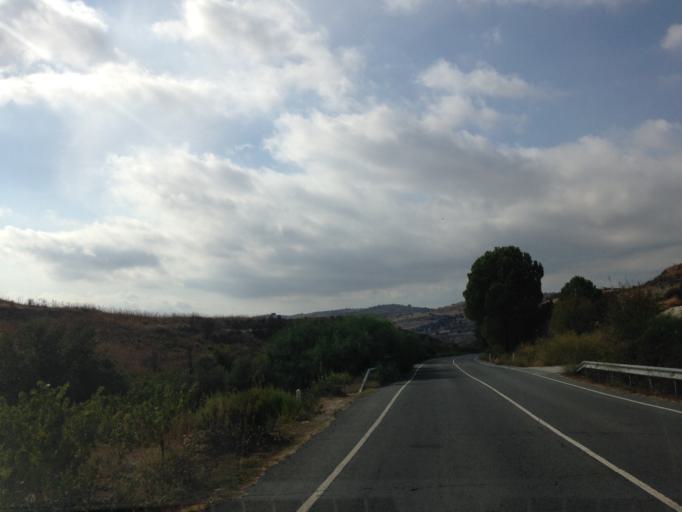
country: CY
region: Limassol
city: Pachna
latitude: 34.7982
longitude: 32.8004
